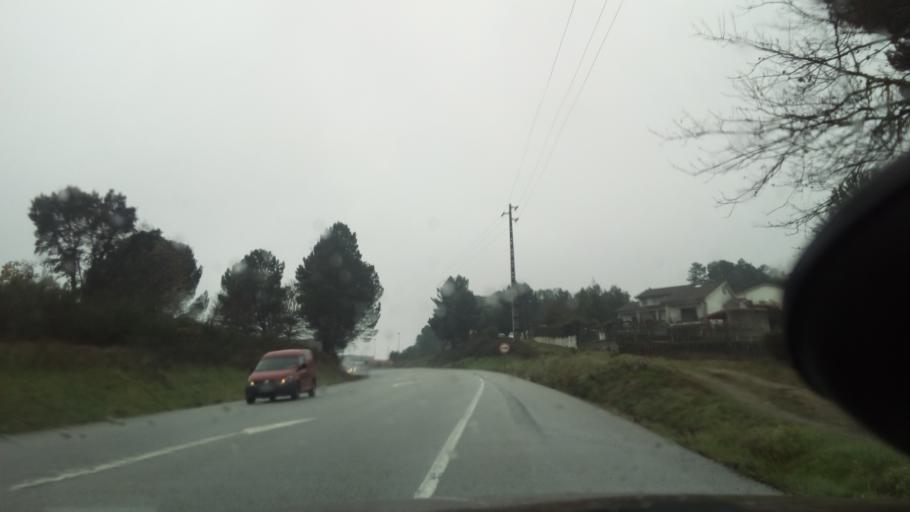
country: PT
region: Viseu
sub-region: Mangualde
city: Mangualde
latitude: 40.6143
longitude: -7.7724
